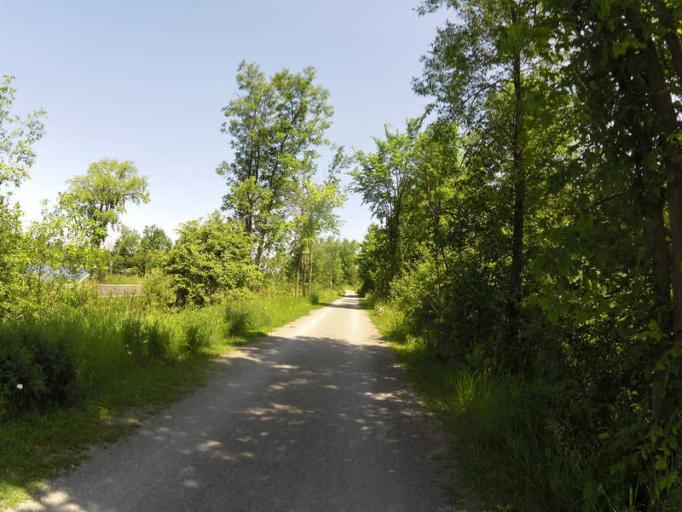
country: CA
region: Ontario
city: Peterborough
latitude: 44.4079
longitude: -78.2615
